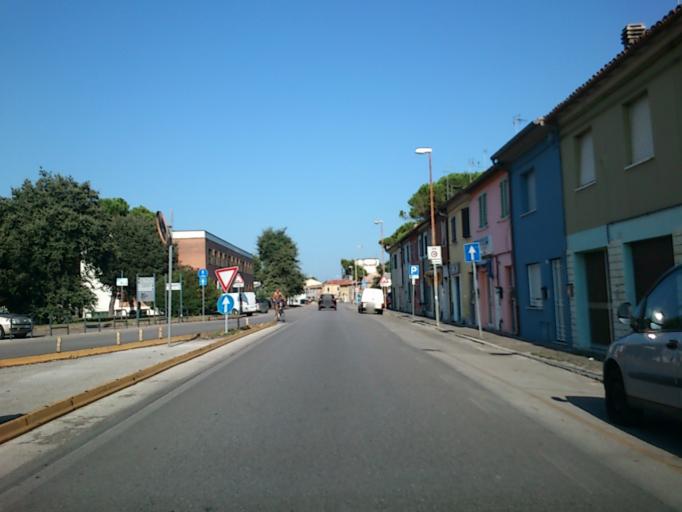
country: IT
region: The Marches
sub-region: Provincia di Pesaro e Urbino
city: Fano
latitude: 43.8394
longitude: 13.0168
